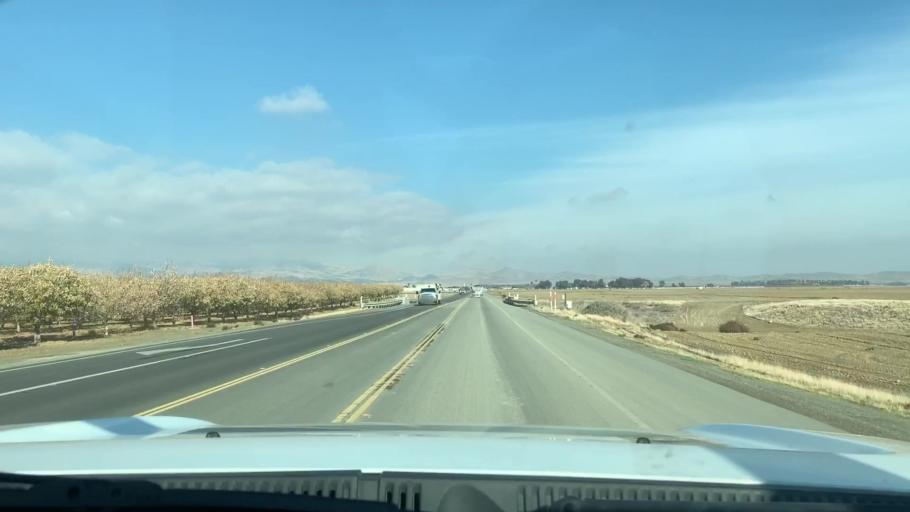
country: US
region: California
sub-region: Fresno County
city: Coalinga
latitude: 36.1675
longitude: -120.3546
